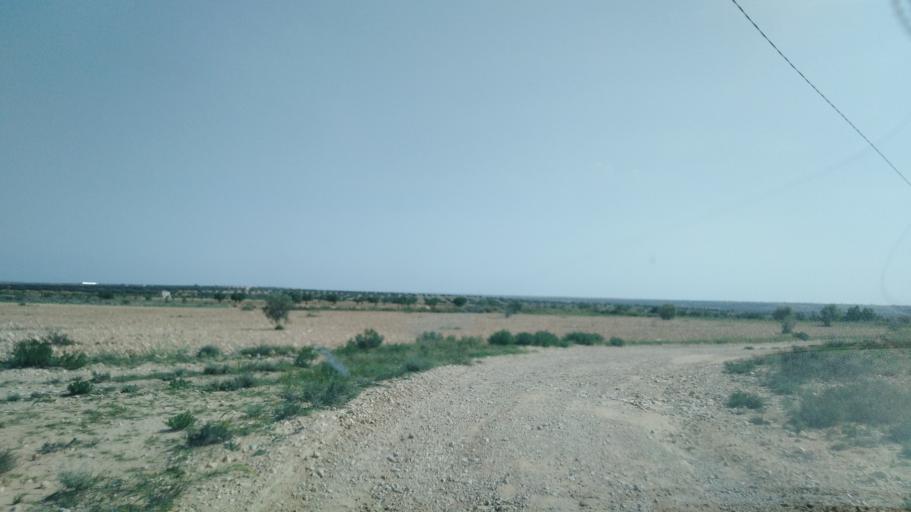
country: TN
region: Safaqis
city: Bi'r `Ali Bin Khalifah
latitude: 34.7964
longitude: 10.3744
